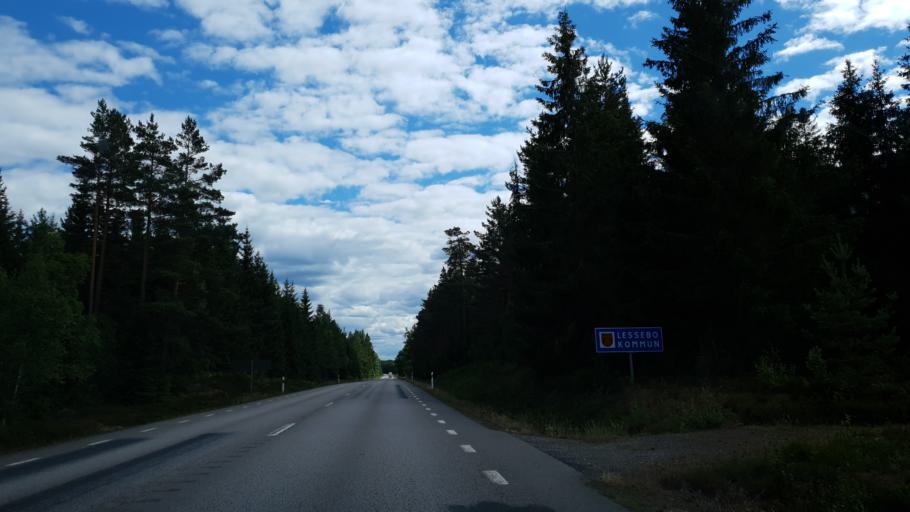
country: SE
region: Kronoberg
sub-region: Uppvidinge Kommun
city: Lenhovda
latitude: 56.8892
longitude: 15.3735
